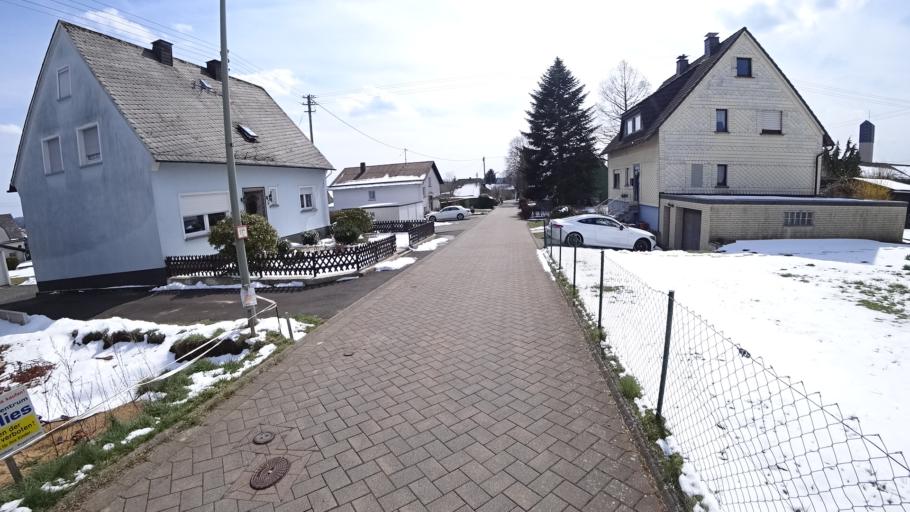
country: DE
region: Rheinland-Pfalz
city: Morlen
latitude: 50.7015
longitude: 7.8788
